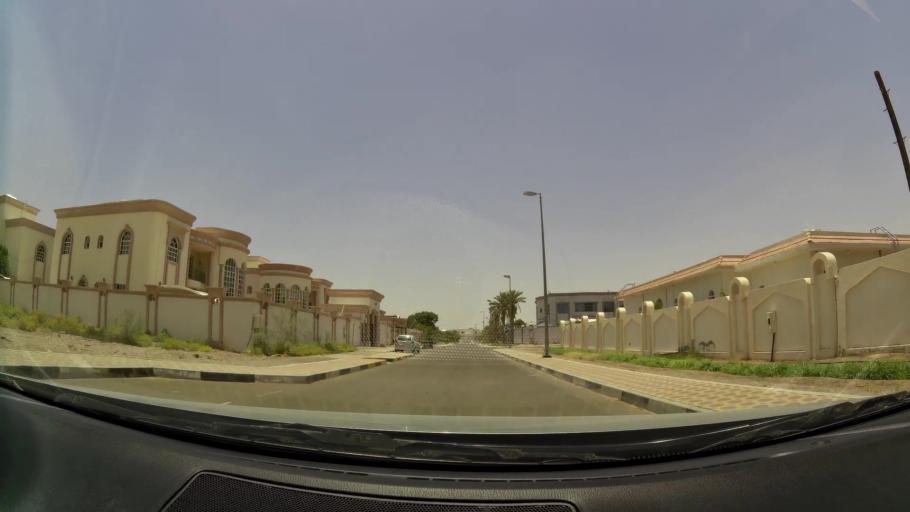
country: OM
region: Al Buraimi
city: Al Buraymi
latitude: 24.2692
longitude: 55.7245
